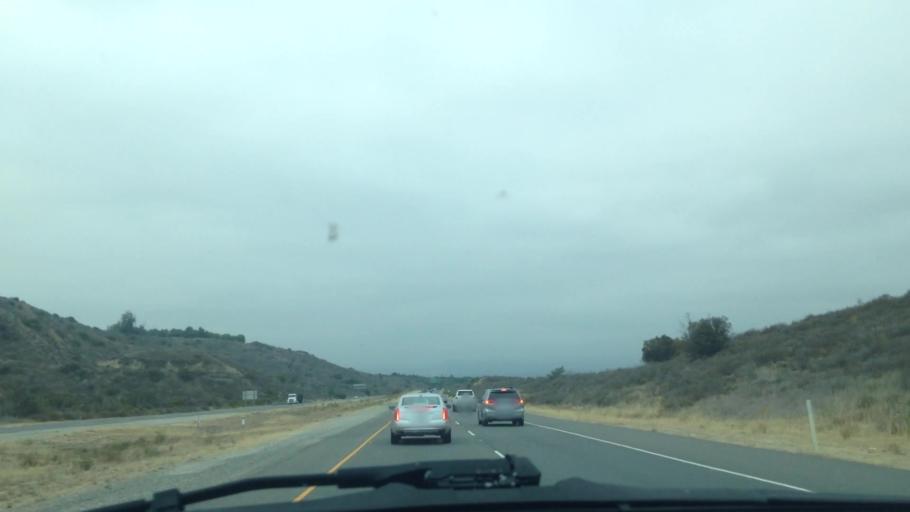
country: US
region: California
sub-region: Orange County
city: North Tustin
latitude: 33.7723
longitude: -117.7587
